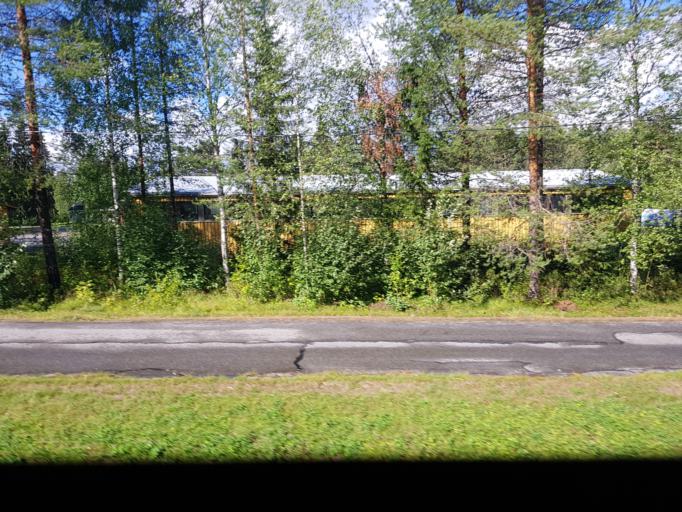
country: FI
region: Kainuu
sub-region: Kehys-Kainuu
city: Kuhmo
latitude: 64.1197
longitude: 29.5028
